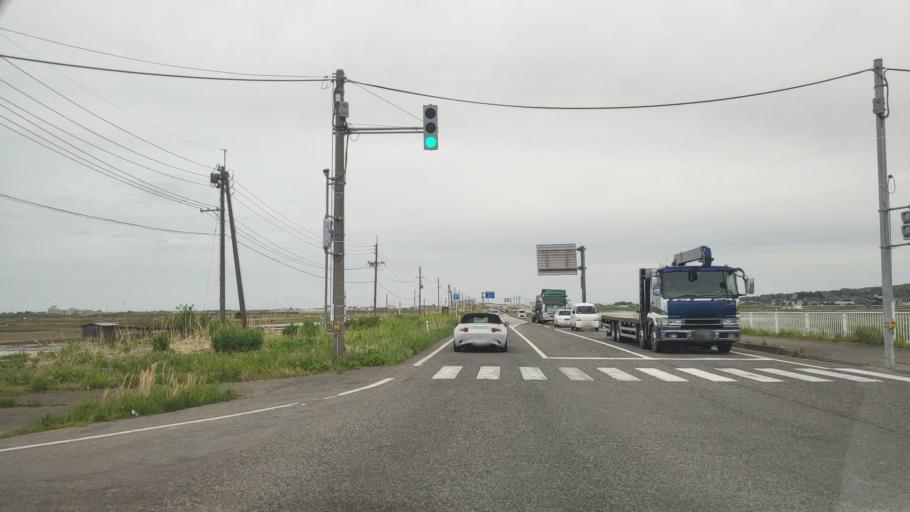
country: JP
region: Niigata
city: Niitsu-honcho
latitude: 37.7711
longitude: 139.1027
